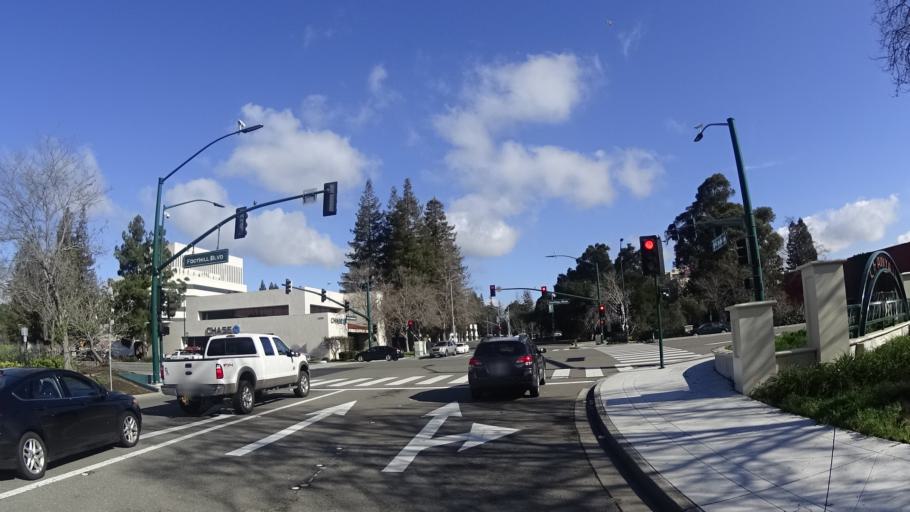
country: US
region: California
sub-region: Alameda County
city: Hayward
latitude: 37.6770
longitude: -122.0836
